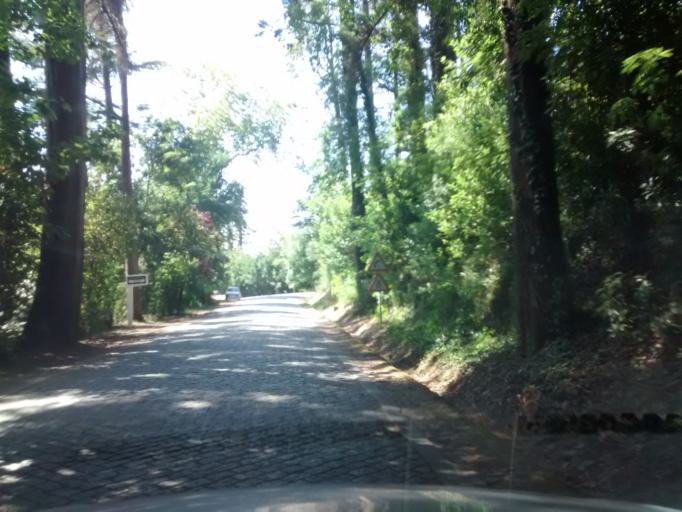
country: PT
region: Aveiro
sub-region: Mealhada
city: Pampilhosa do Botao
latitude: 40.3795
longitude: -8.3712
